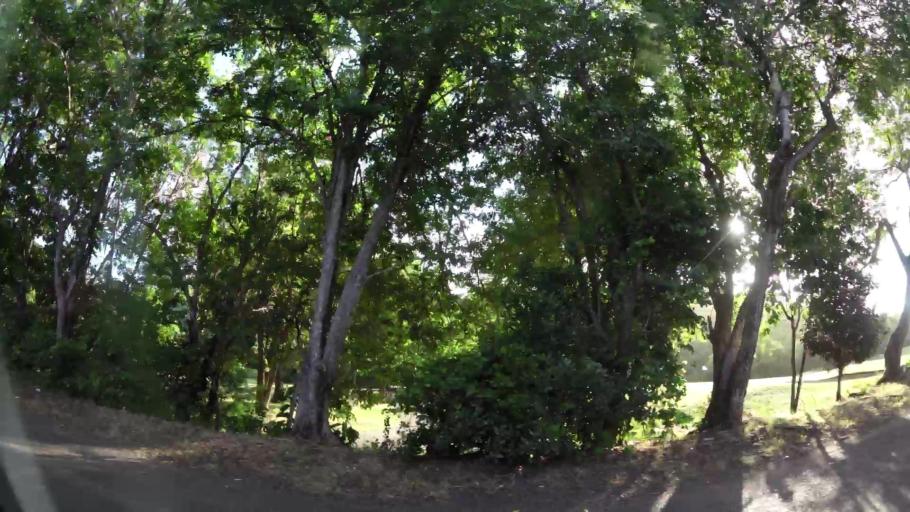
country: LC
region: Gros-Islet
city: Gros Islet
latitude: 14.0967
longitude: -60.9385
